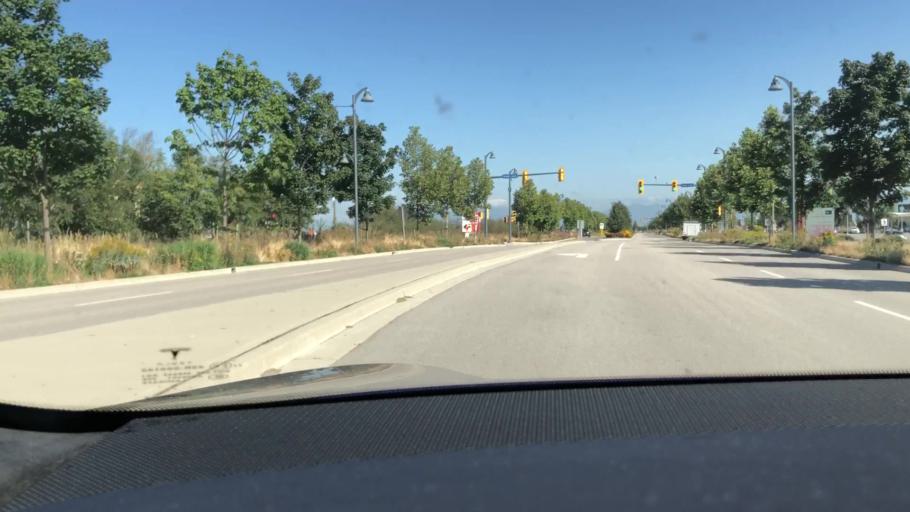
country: US
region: Washington
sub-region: Whatcom County
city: Point Roberts
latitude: 49.0342
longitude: -123.0903
